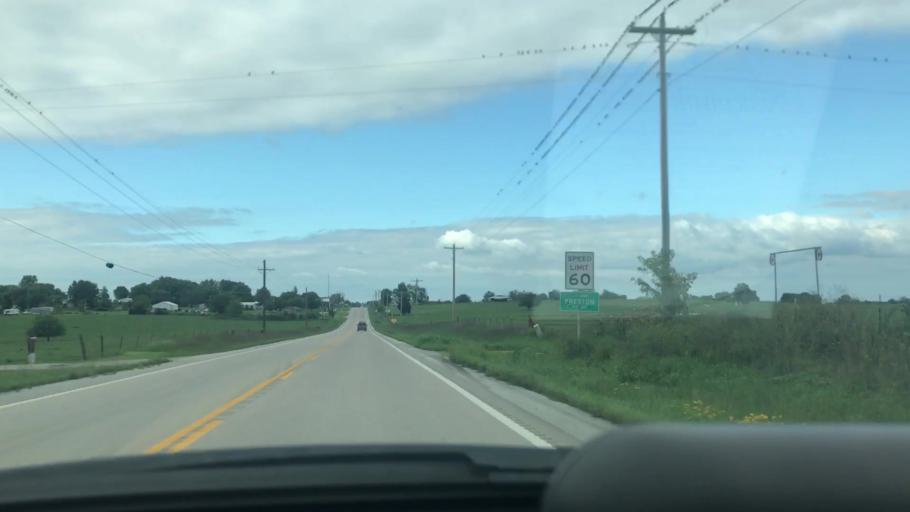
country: US
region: Missouri
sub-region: Hickory County
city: Hermitage
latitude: 37.9334
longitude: -93.2085
